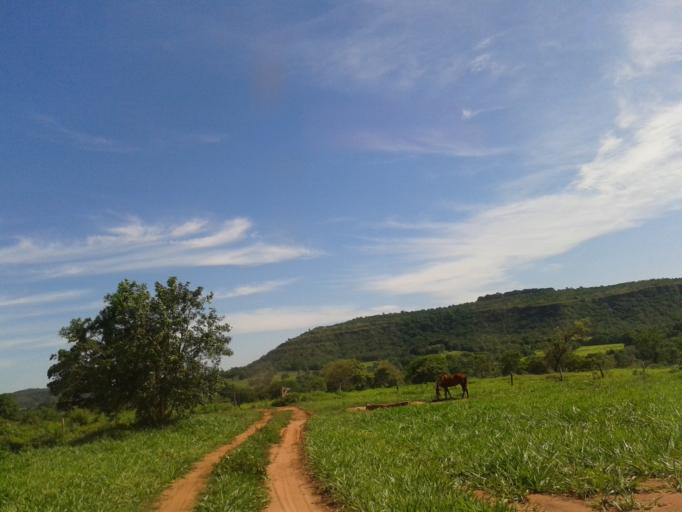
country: BR
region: Minas Gerais
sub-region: Santa Vitoria
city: Santa Vitoria
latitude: -19.0965
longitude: -50.0123
